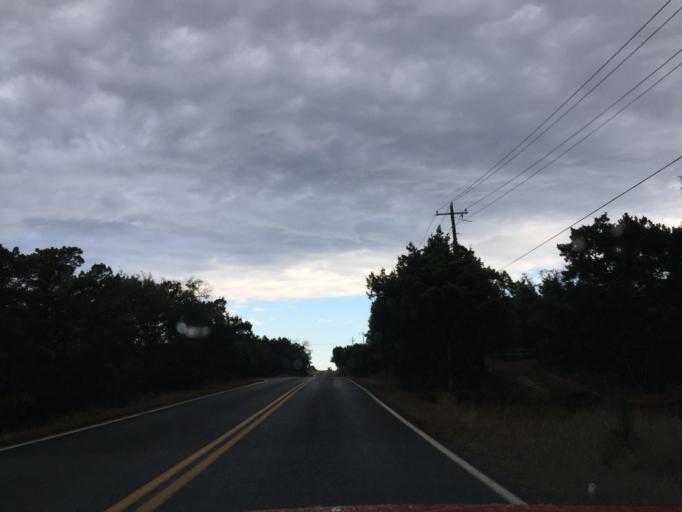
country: US
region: Texas
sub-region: Williamson County
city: Leander
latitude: 30.6170
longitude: -97.9424
